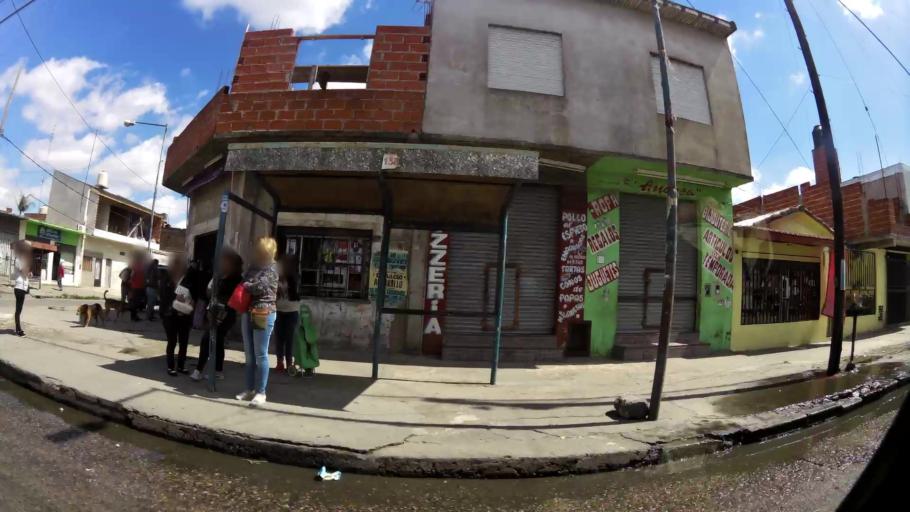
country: AR
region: Buenos Aires F.D.
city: Villa Lugano
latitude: -34.6749
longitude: -58.4298
